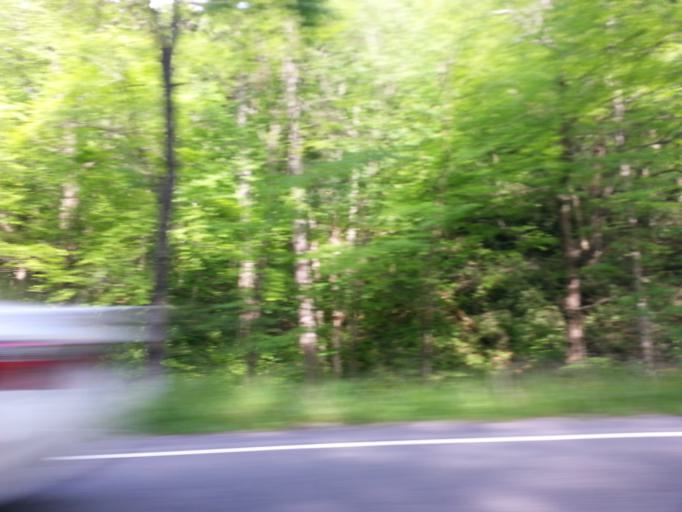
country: US
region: Tennessee
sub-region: Sevier County
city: Gatlinburg
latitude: 35.6229
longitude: -83.4216
